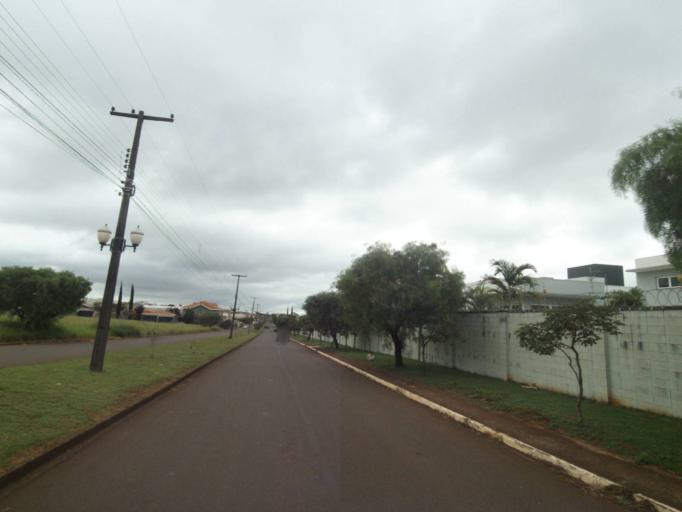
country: BR
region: Parana
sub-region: Campo Mourao
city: Campo Mourao
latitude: -24.0336
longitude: -52.3608
